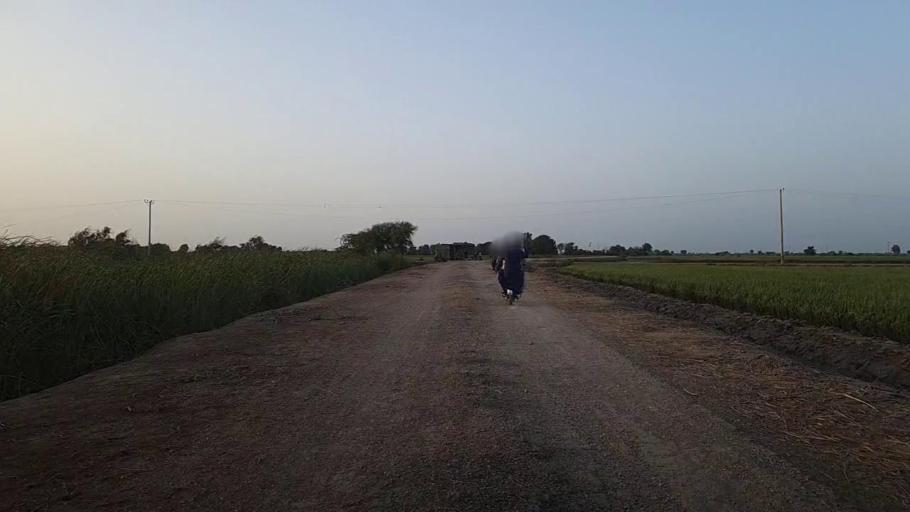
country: PK
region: Sindh
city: Kario
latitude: 24.7295
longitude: 68.4604
